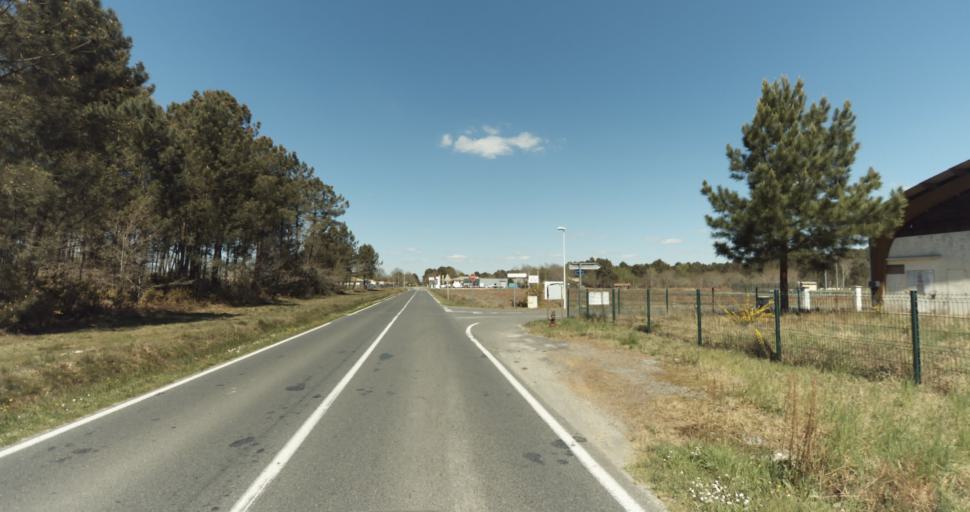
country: FR
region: Aquitaine
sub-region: Departement de la Gironde
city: Martignas-sur-Jalle
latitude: 44.7978
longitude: -0.7774
